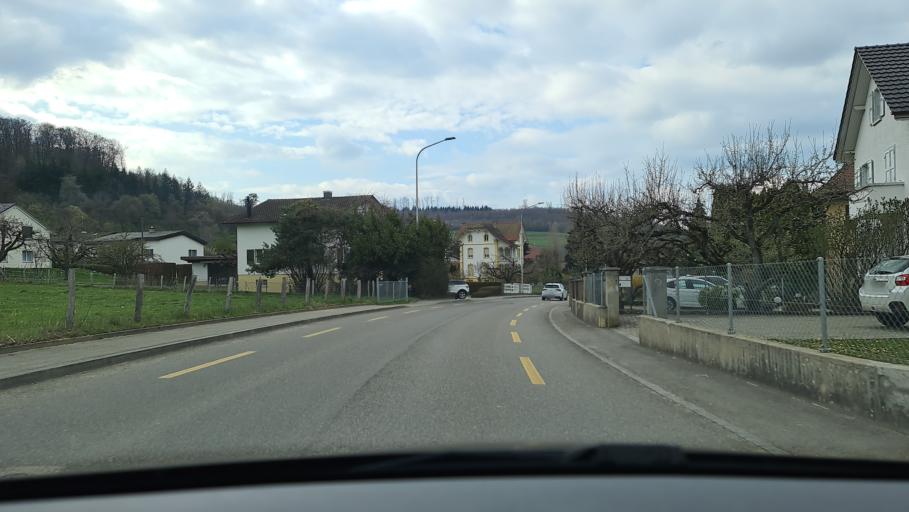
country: CH
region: Jura
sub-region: Porrentruy District
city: Porrentruy
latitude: 47.4541
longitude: 7.0506
